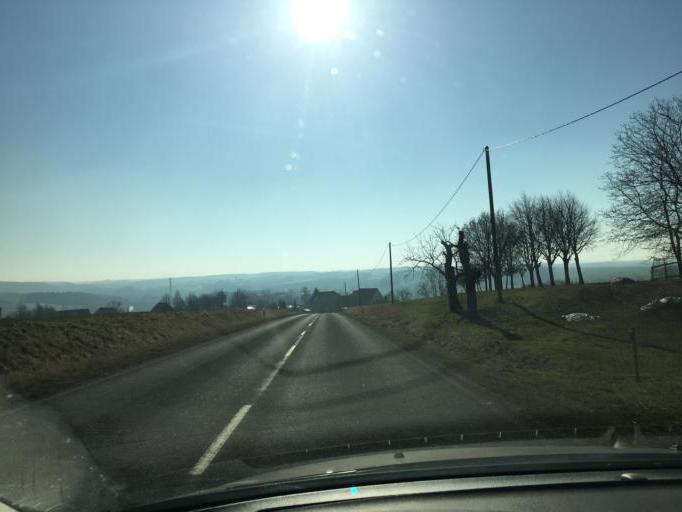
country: DE
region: Saxony
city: Lunzenau
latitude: 50.9695
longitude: 12.7468
